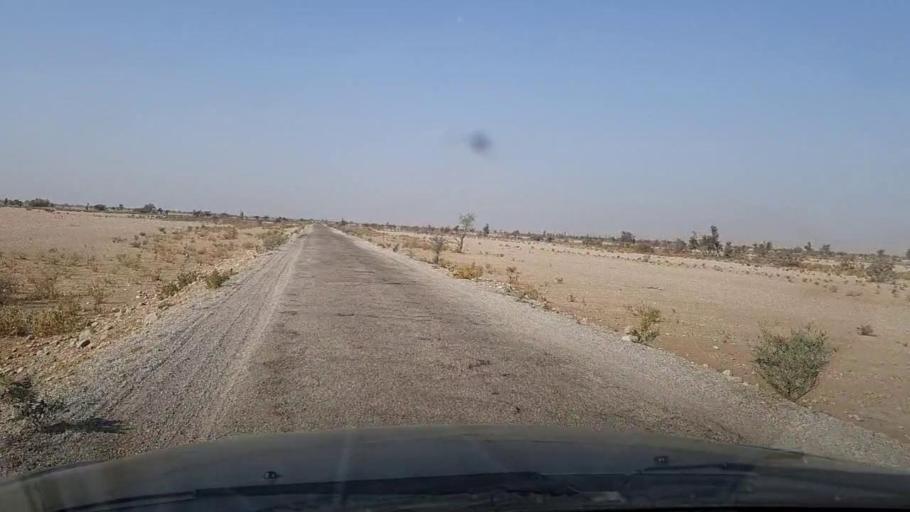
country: PK
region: Sindh
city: Sann
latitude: 25.9172
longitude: 68.0126
